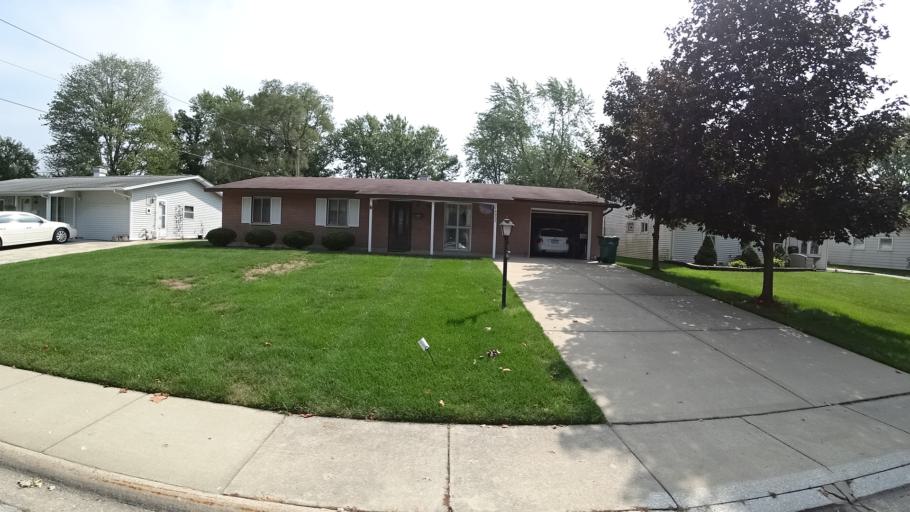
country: US
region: Illinois
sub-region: Cook County
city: Orland Park
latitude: 41.6182
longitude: -87.8667
